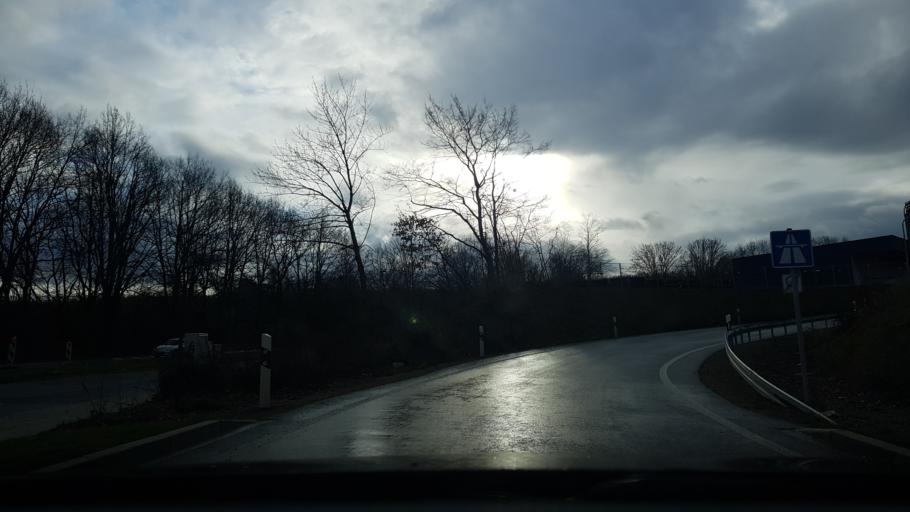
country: DE
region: North Rhine-Westphalia
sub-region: Regierungsbezirk Arnsberg
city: Bochum
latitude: 51.4625
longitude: 7.2633
